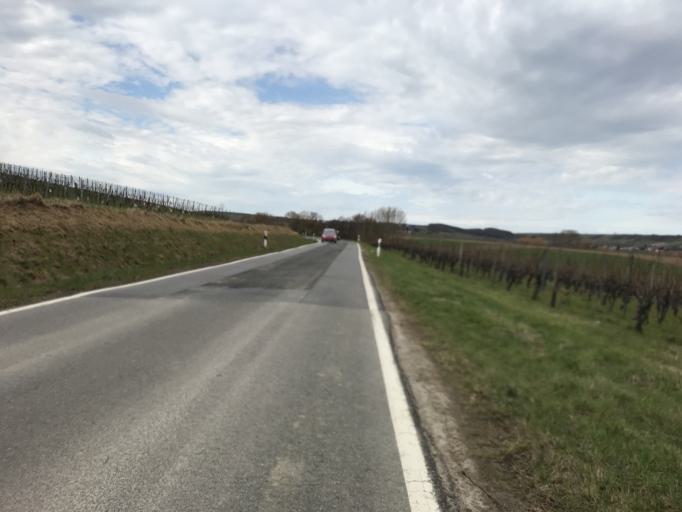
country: DE
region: Rheinland-Pfalz
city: Stadecken-Elsheim
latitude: 49.8880
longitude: 8.1129
